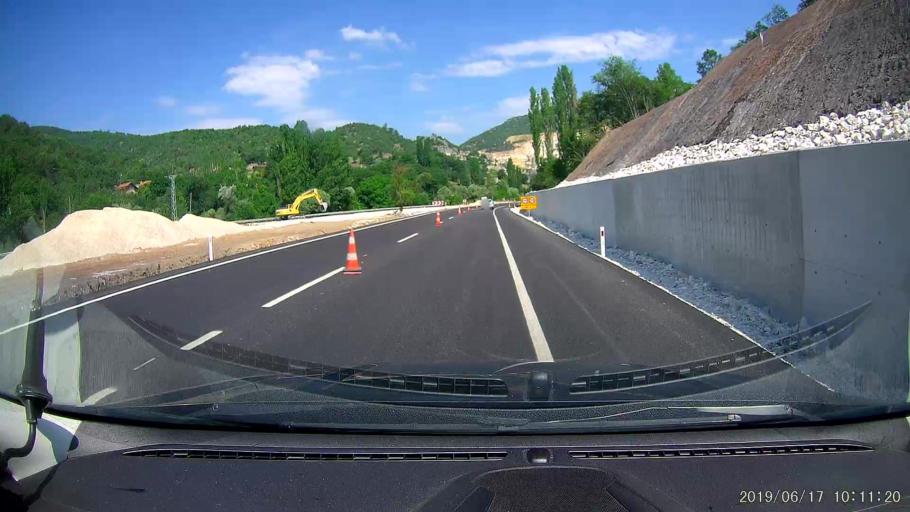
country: TR
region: Amasya
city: Saraycik
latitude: 40.9698
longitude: 35.0849
